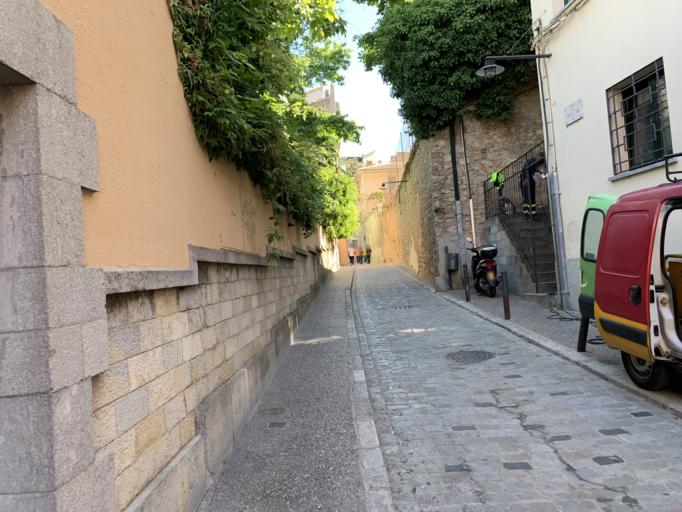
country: ES
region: Catalonia
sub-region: Provincia de Girona
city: Girona
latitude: 41.9830
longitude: 2.8265
